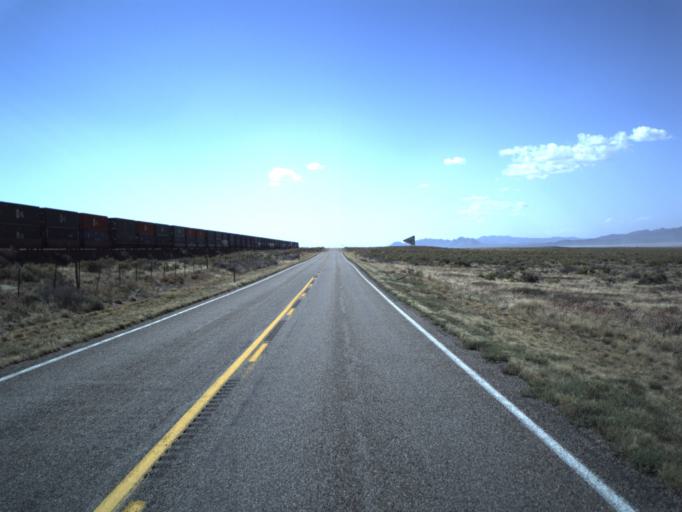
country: US
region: Utah
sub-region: Beaver County
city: Milford
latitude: 38.6818
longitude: -112.9778
